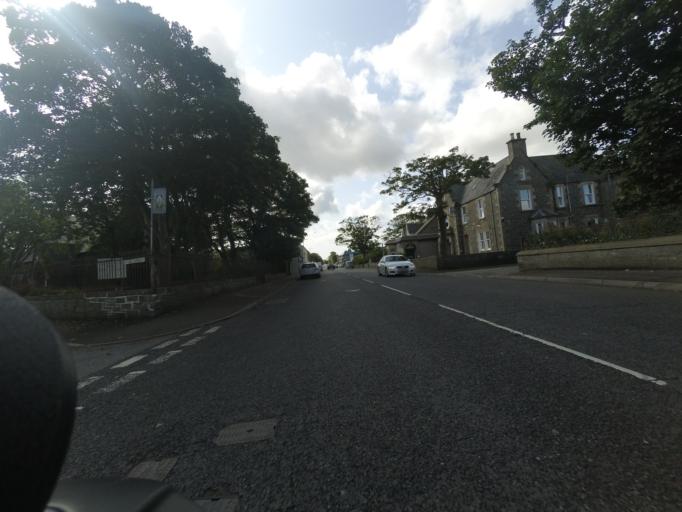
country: GB
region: Scotland
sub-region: Highland
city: Wick
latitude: 58.4386
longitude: -3.0940
